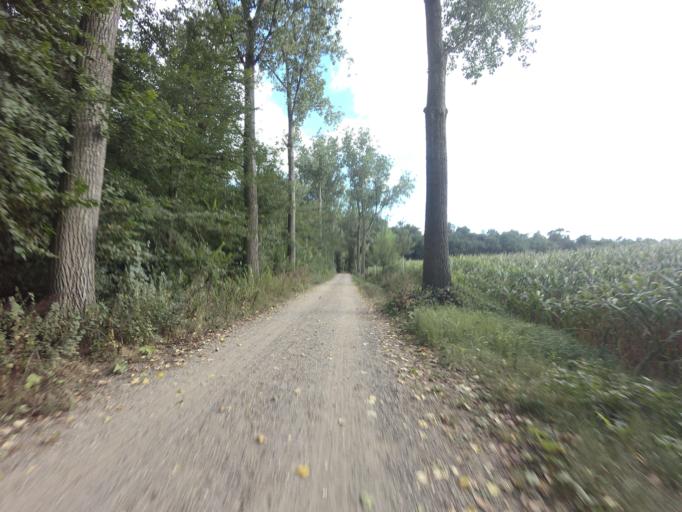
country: NL
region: North Brabant
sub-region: Gemeente Grave
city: Grave
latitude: 51.7346
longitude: 5.7415
